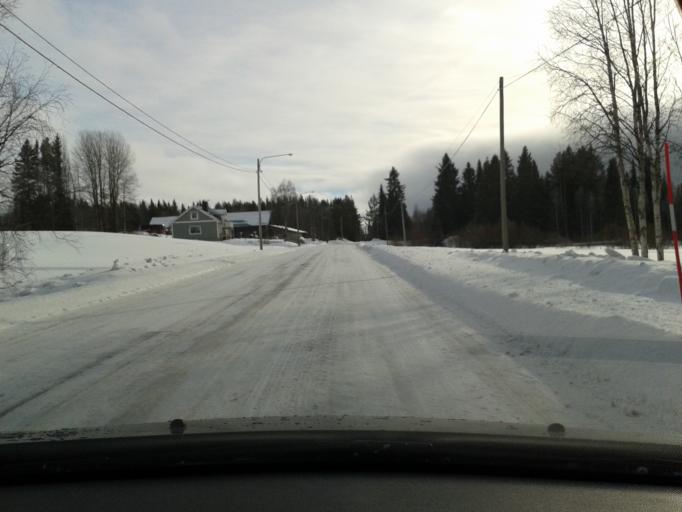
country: SE
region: Vaesterbotten
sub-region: Vilhelmina Kommun
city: Sjoberg
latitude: 64.6904
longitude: 16.2706
